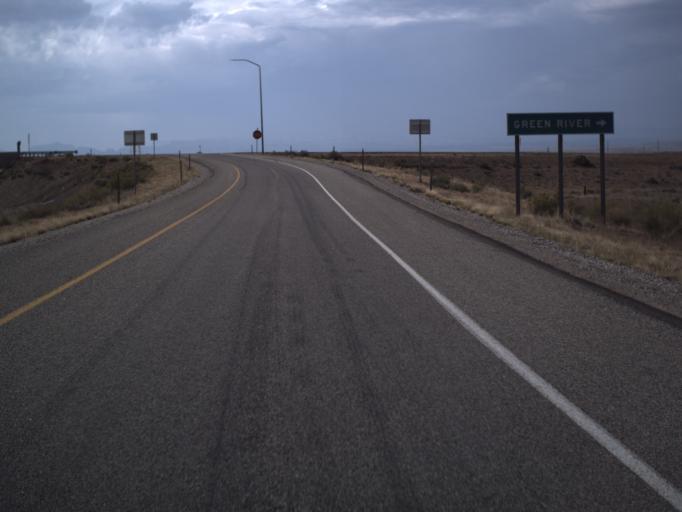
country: US
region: Utah
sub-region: Carbon County
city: East Carbon City
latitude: 38.9763
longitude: -110.1189
